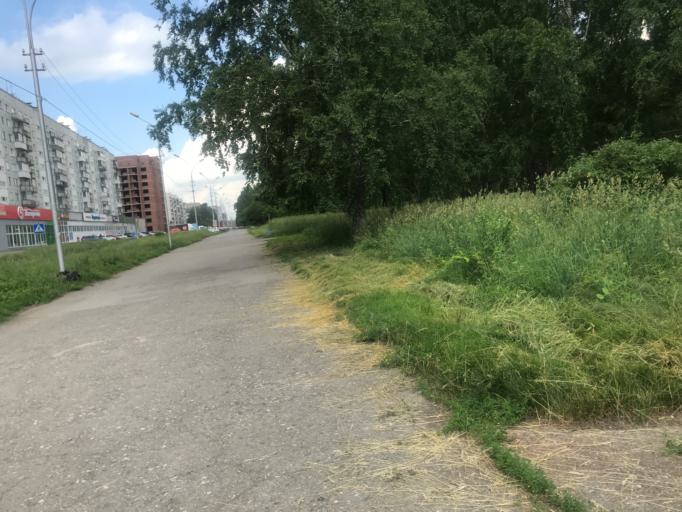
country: RU
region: Novosibirsk
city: Krasnoobsk
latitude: 54.9402
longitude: 82.9148
